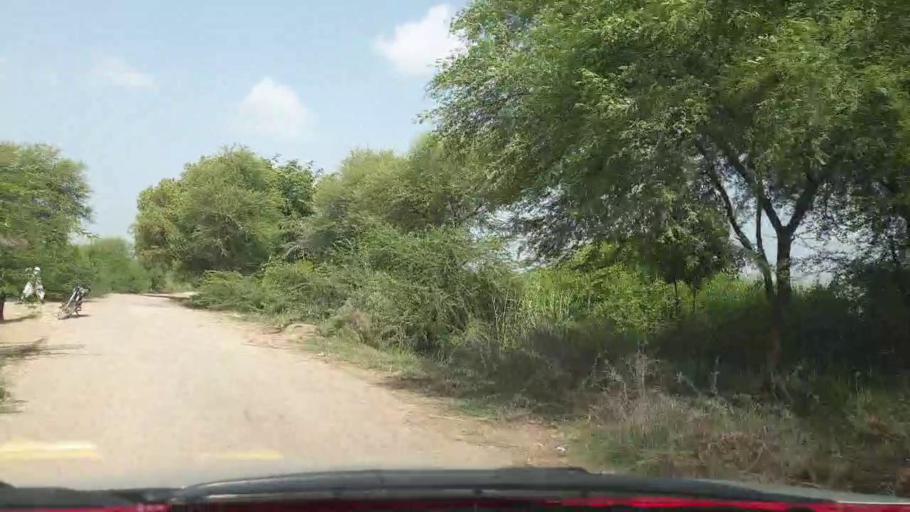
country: PK
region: Sindh
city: Tando Bago
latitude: 24.8652
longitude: 68.9236
